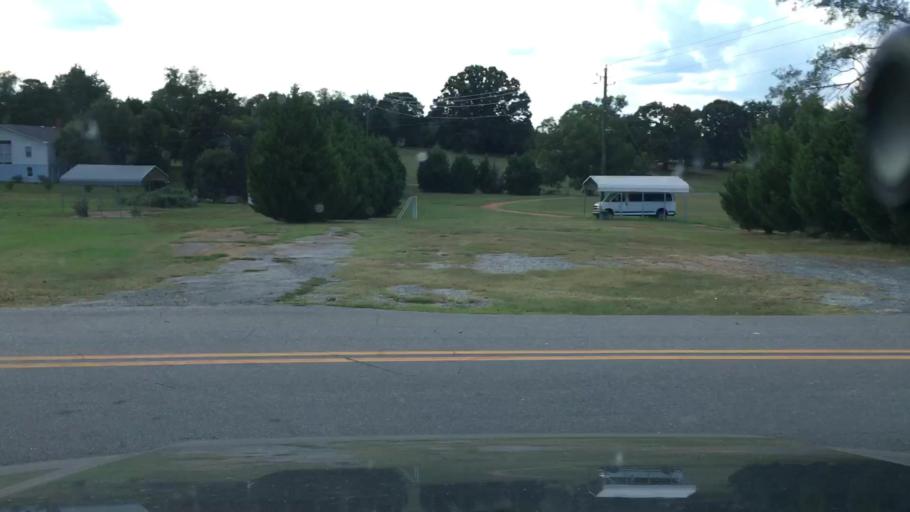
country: US
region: Georgia
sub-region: Monroe County
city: Forsyth
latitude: 32.9823
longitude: -83.8769
